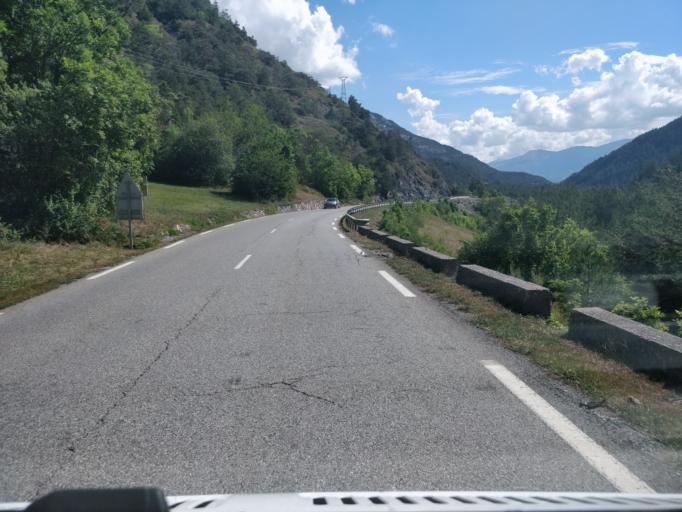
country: FR
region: Provence-Alpes-Cote d'Azur
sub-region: Departement des Alpes-de-Haute-Provence
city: Barcelonnette
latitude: 44.4008
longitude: 6.5179
